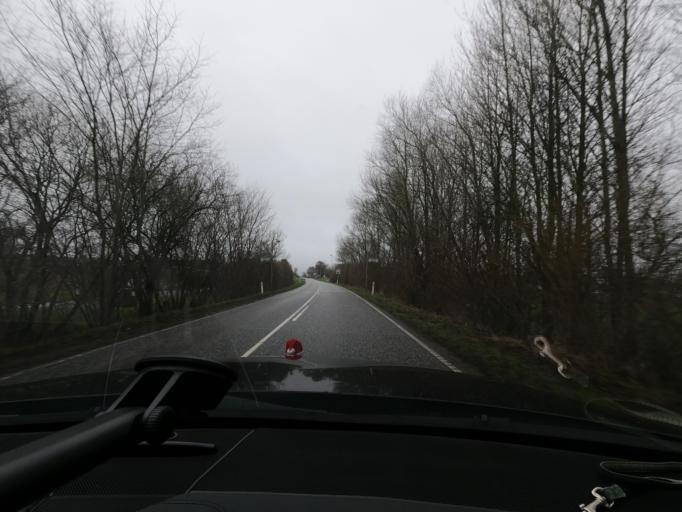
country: DK
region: South Denmark
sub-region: Sonderborg Kommune
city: Broager
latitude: 54.9234
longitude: 9.6833
